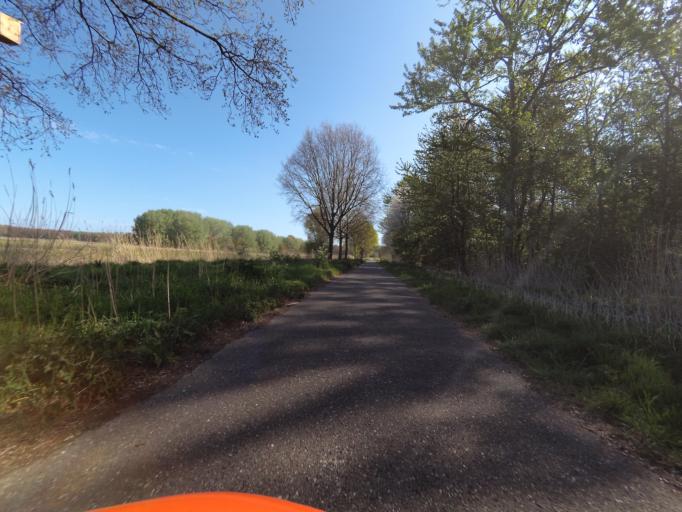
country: NL
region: Flevoland
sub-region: Gemeente Almere
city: Almere Stad
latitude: 52.3709
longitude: 5.1645
